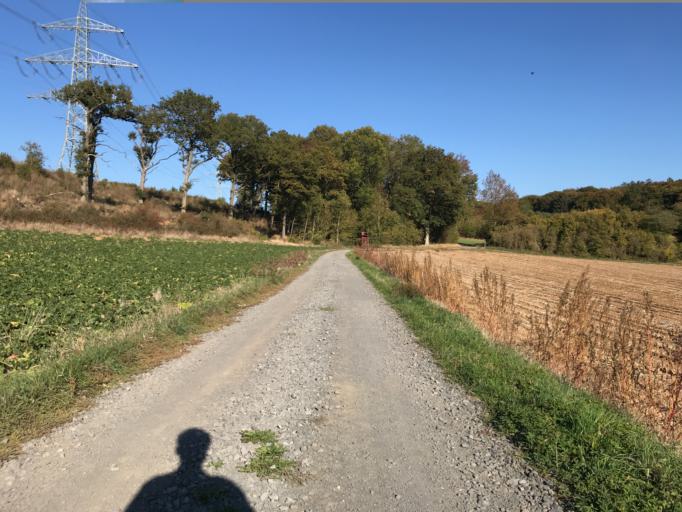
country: DE
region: Rheinland-Pfalz
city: Wolken
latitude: 50.3363
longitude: 7.4431
